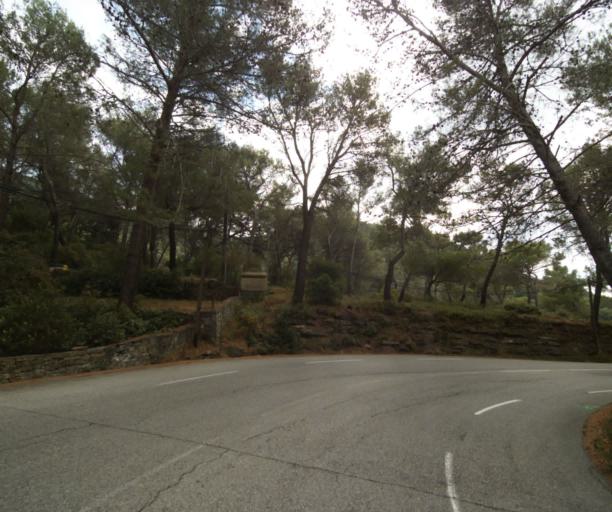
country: FR
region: Provence-Alpes-Cote d'Azur
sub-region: Departement des Bouches-du-Rhone
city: Ceyreste
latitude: 43.2309
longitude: 5.6585
